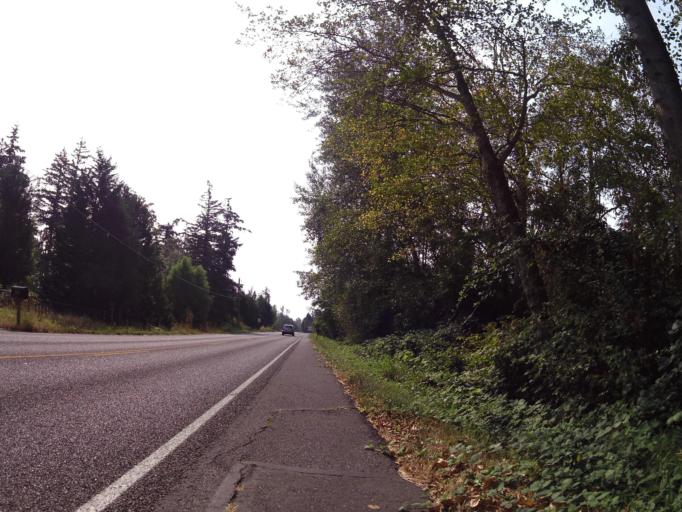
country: US
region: Washington
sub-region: Whatcom County
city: Marietta-Alderwood
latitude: 48.7853
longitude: -122.5560
